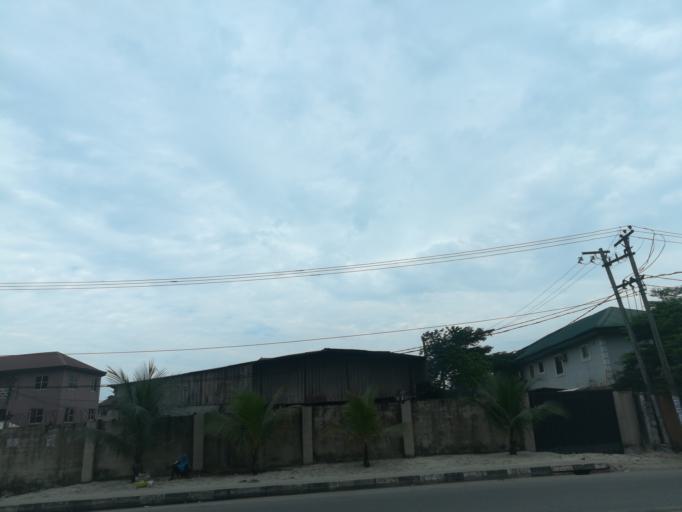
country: NG
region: Rivers
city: Port Harcourt
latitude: 4.8345
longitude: 6.9766
